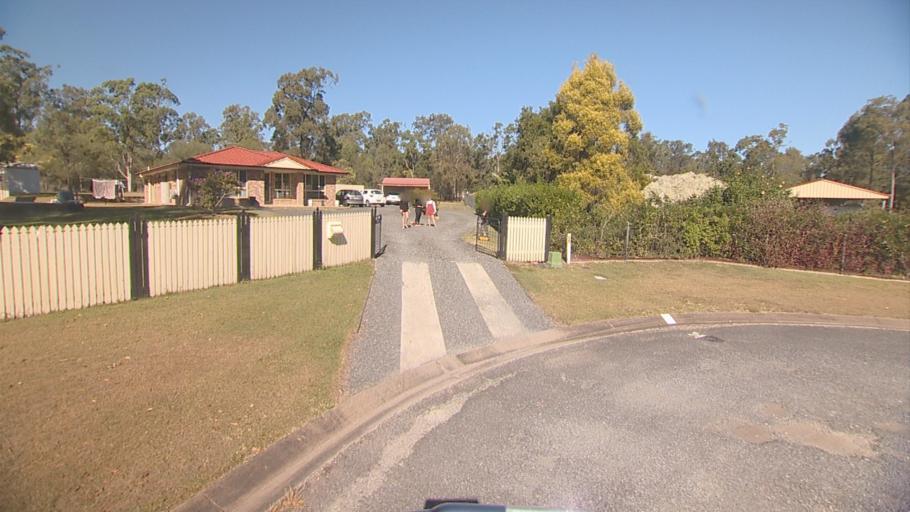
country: AU
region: Queensland
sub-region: Logan
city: North Maclean
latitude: -27.8212
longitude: 152.9498
